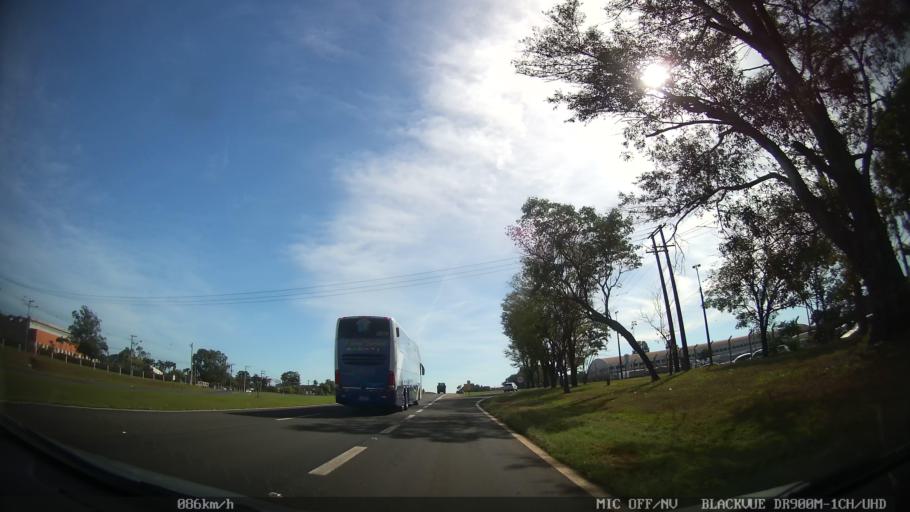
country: BR
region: Sao Paulo
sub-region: Leme
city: Leme
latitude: -22.2054
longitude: -47.3949
